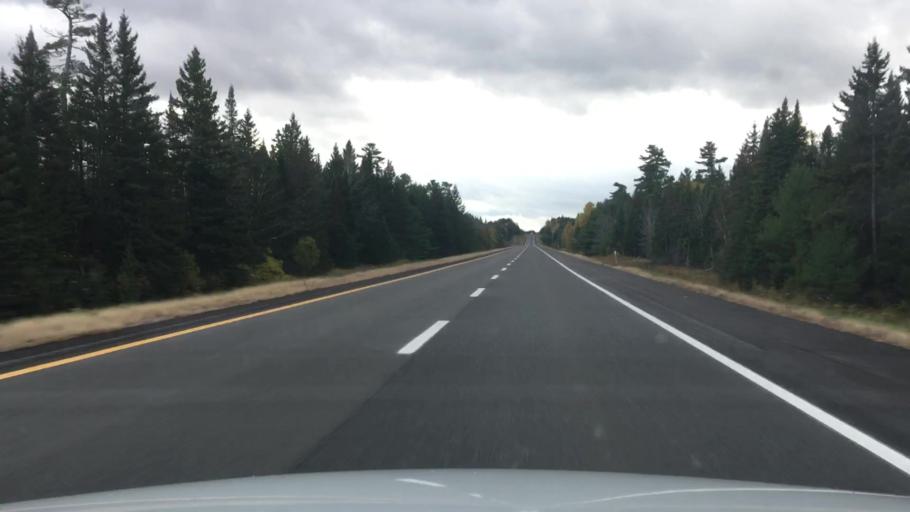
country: US
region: Maine
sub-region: Penobscot County
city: Patten
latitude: 46.0703
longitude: -68.2244
